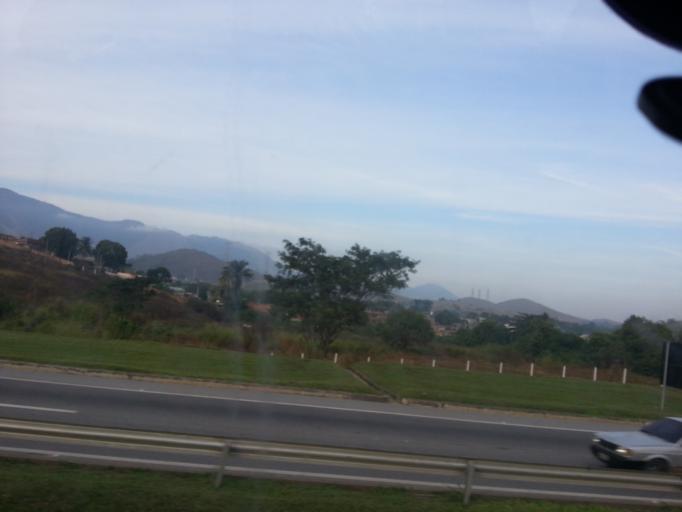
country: BR
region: Rio de Janeiro
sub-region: Queimados
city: Queimados
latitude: -22.7412
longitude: -43.5226
